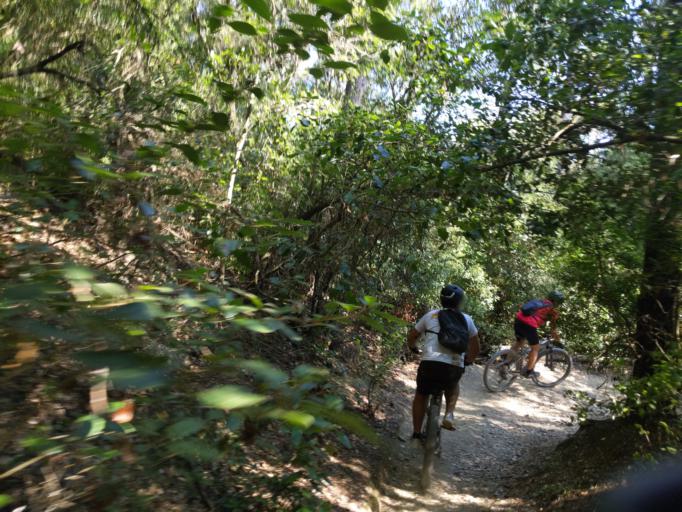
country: ES
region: Catalonia
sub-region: Provincia de Barcelona
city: Cerdanyola del Valles
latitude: 41.4703
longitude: 2.1291
